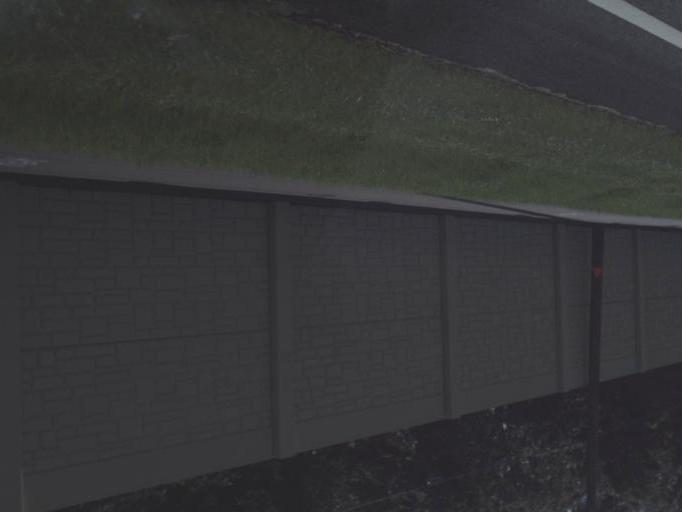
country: US
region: Florida
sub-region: Collier County
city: Lely Resort
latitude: 26.0441
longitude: -81.6696
